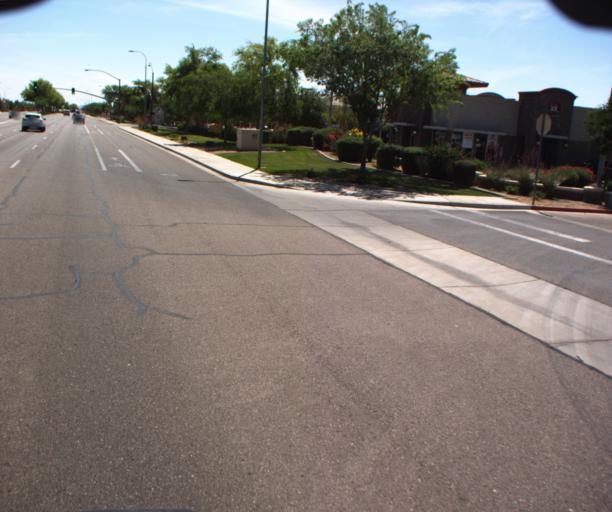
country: US
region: Arizona
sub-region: Maricopa County
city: Sun Lakes
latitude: 33.2451
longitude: -111.8414
